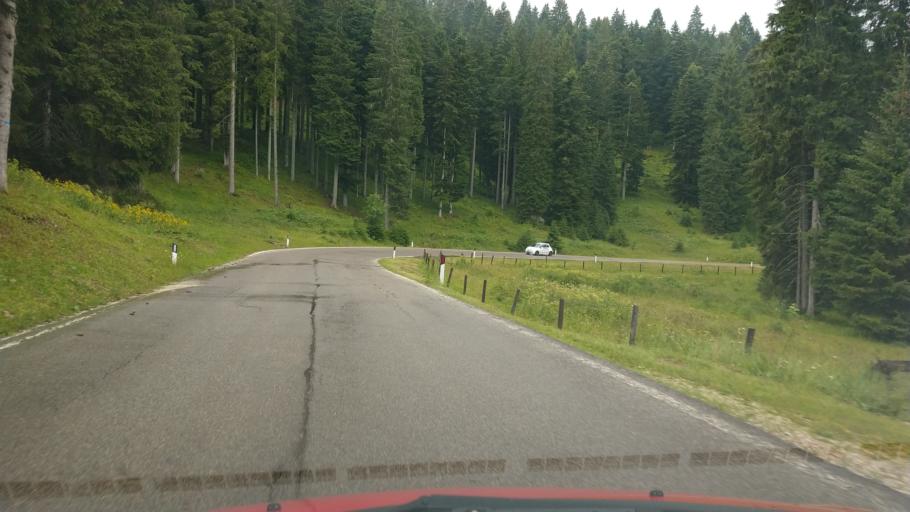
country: IT
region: Veneto
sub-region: Provincia di Vicenza
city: Lastebasse
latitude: 45.9002
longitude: 11.2476
